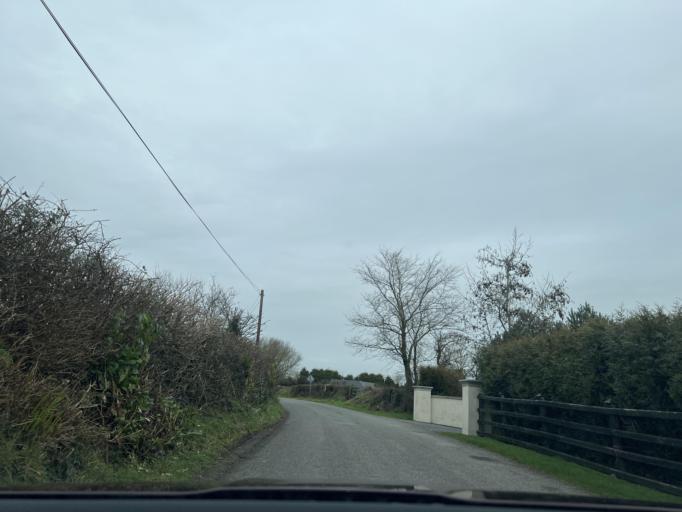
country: IE
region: Leinster
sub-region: Loch Garman
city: Loch Garman
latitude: 52.3612
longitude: -6.5199
